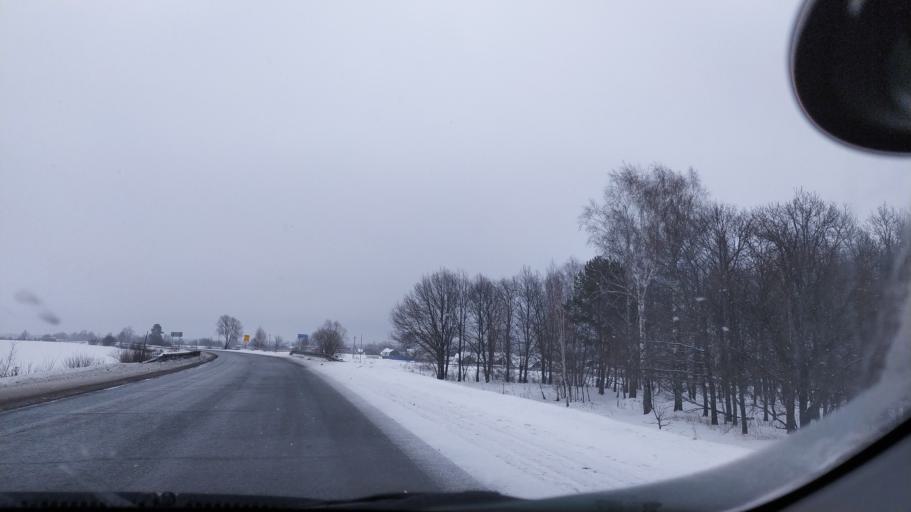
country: RU
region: Mariy-El
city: Krasnogorskiy
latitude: 56.1465
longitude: 48.1236
